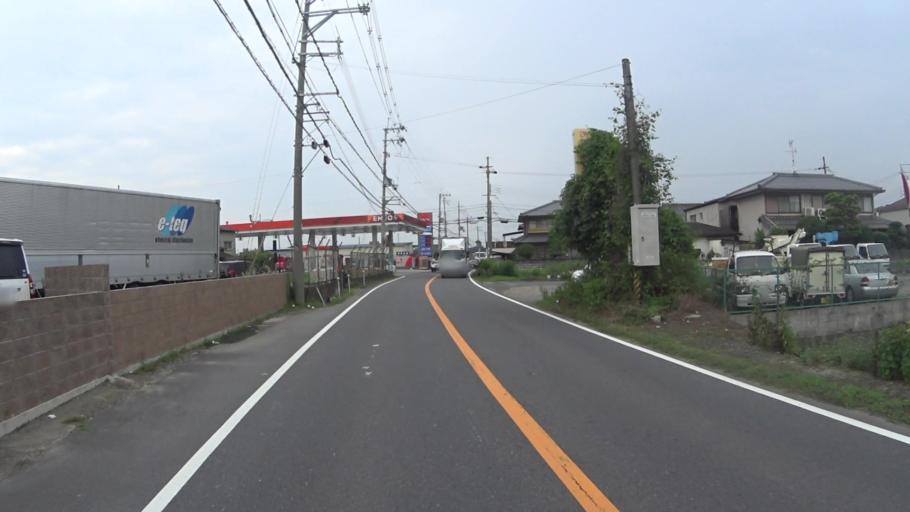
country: JP
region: Kyoto
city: Tanabe
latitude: 34.8519
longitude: 135.7451
